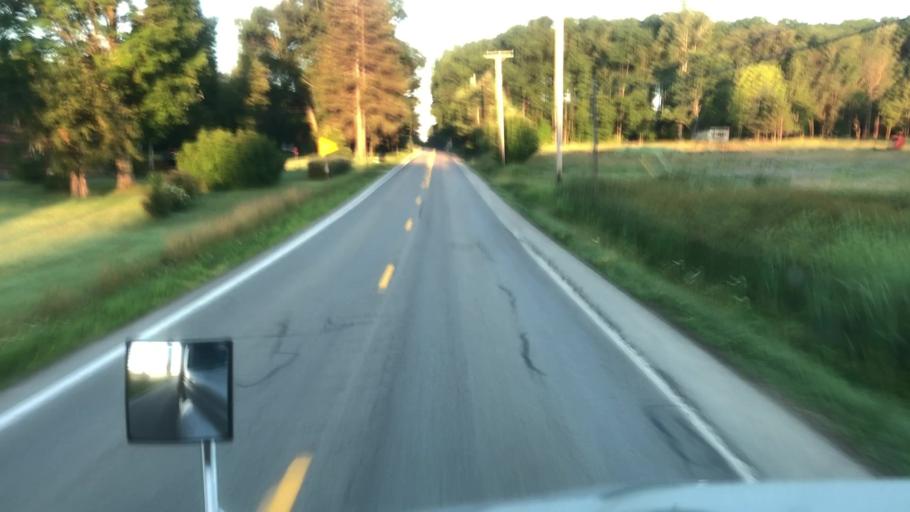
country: US
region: Pennsylvania
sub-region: Crawford County
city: Titusville
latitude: 41.5930
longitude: -79.6051
